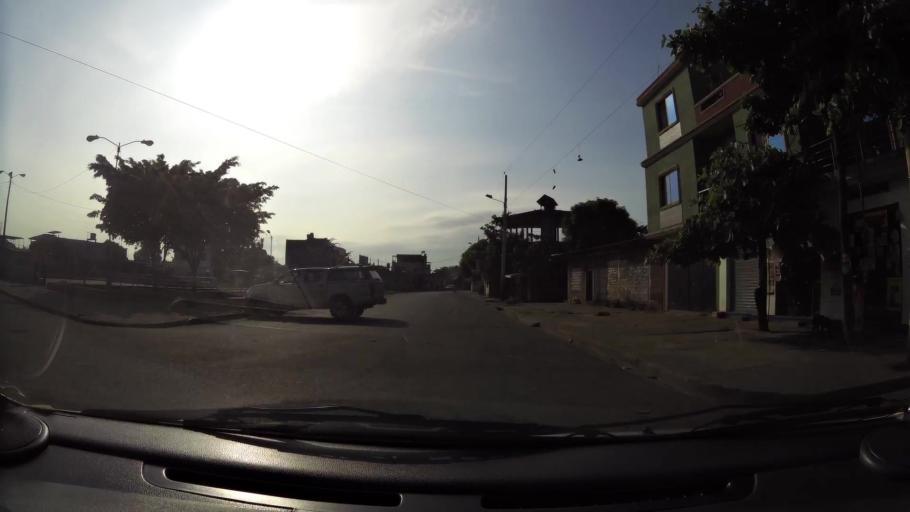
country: EC
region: Guayas
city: Eloy Alfaro
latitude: -2.1838
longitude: -79.8415
